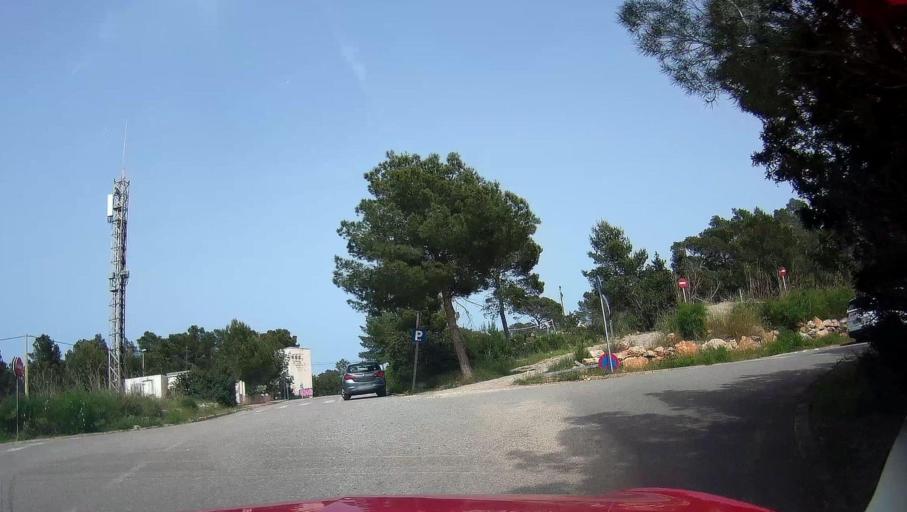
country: ES
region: Balearic Islands
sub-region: Illes Balears
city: Sant Joan de Labritja
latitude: 39.1113
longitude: 1.5194
